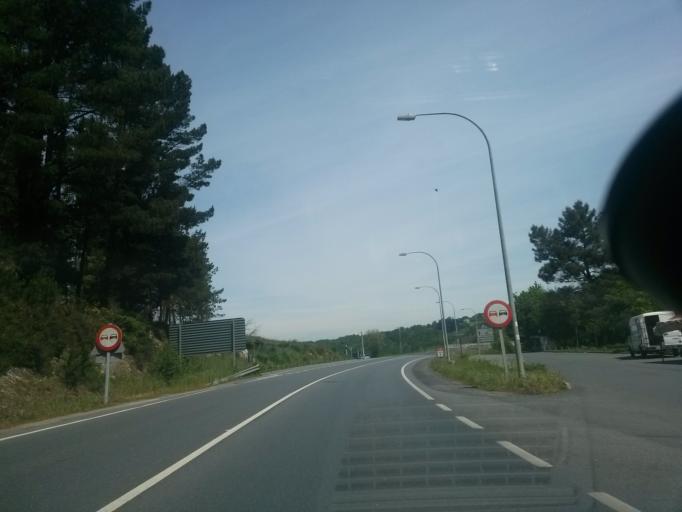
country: ES
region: Galicia
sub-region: Provincia de Lugo
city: Lugo
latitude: 43.0031
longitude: -7.5832
